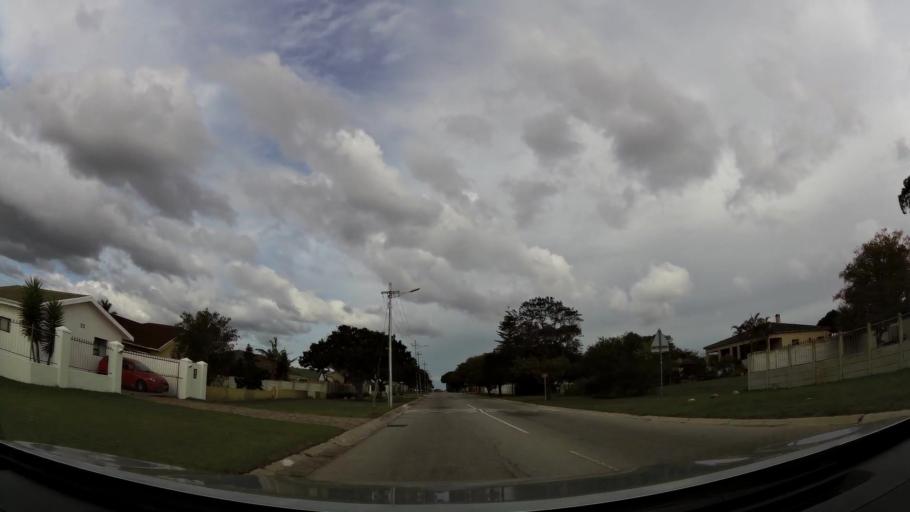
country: ZA
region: Eastern Cape
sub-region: Nelson Mandela Bay Metropolitan Municipality
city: Port Elizabeth
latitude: -33.9412
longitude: 25.5210
